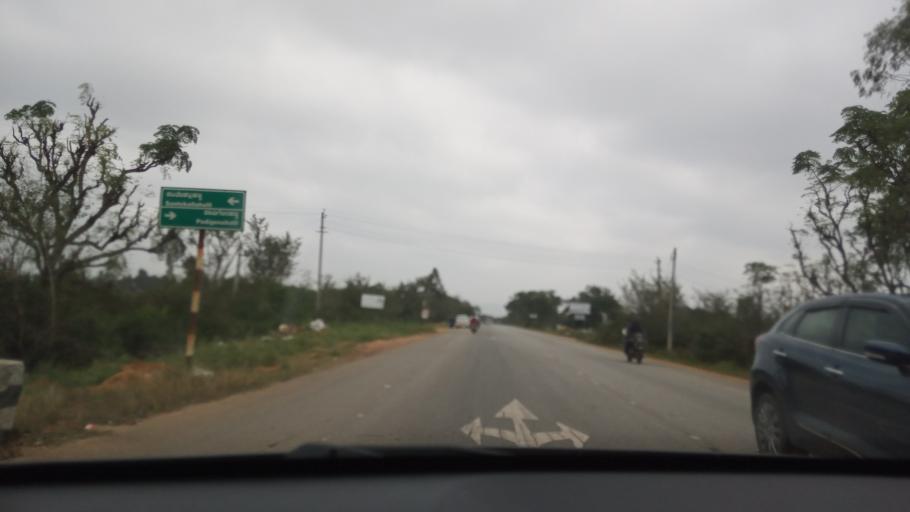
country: IN
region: Karnataka
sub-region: Chikkaballapur
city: Sidlaghatta
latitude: 13.2810
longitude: 77.9566
